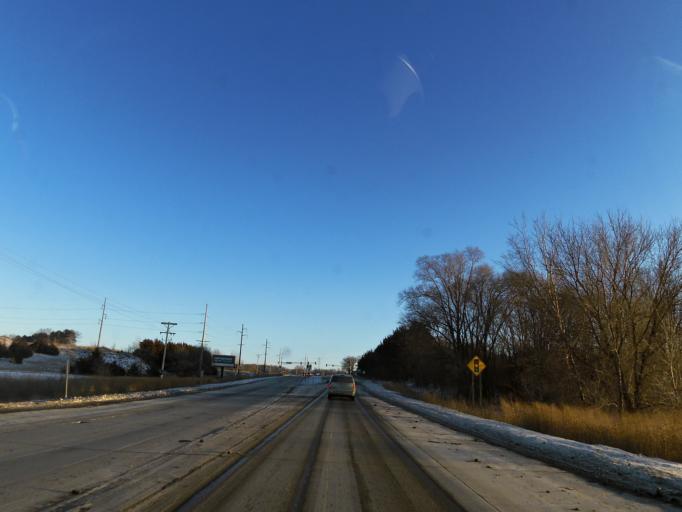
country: US
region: Minnesota
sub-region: Carver County
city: Chaska
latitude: 44.7705
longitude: -93.5844
